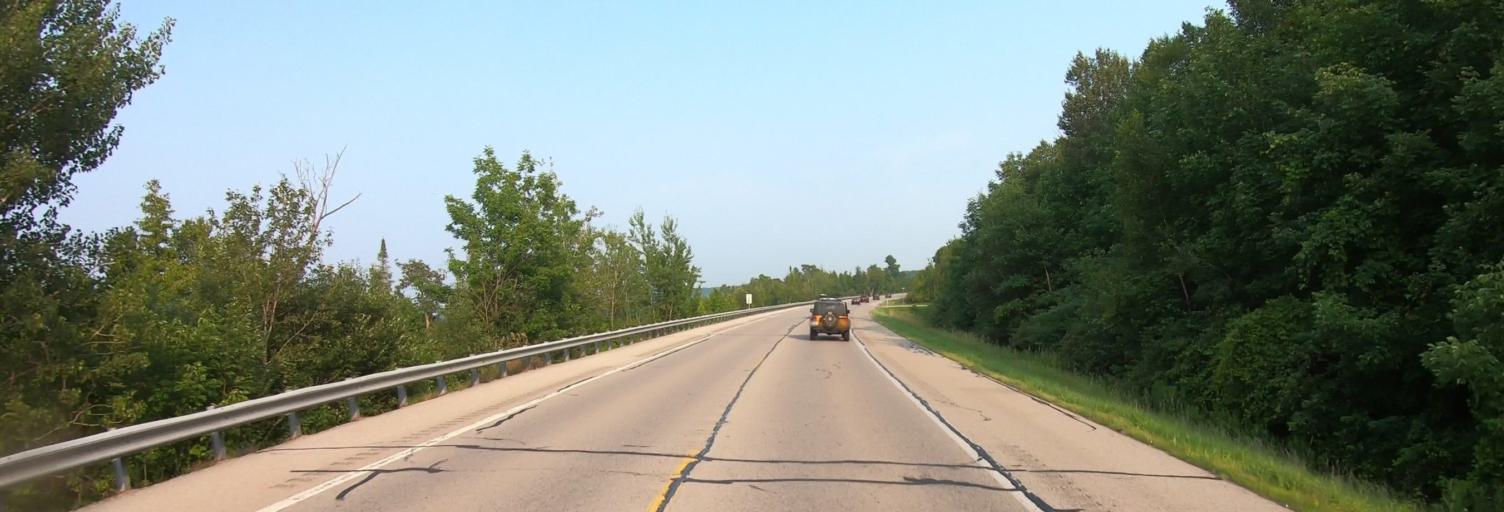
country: US
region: Michigan
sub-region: Charlevoix County
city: Charlevoix
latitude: 45.3677
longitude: -85.1291
